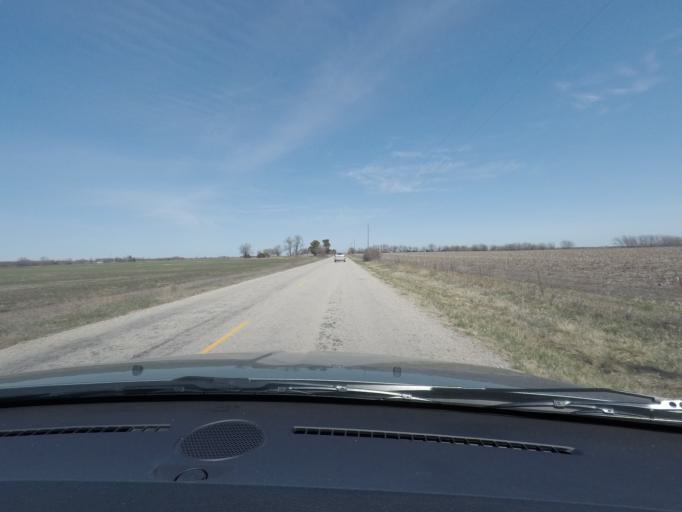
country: US
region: Kansas
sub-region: Lyon County
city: Emporia
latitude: 38.5429
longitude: -96.1700
